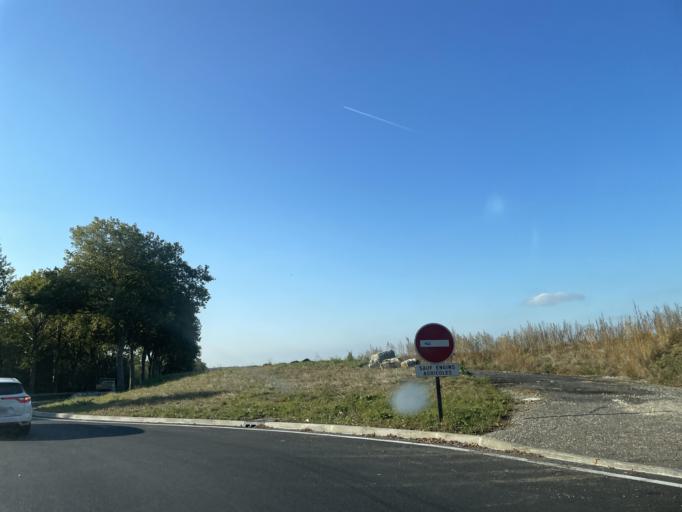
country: FR
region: Ile-de-France
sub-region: Departement de Seine-et-Marne
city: La Chapelle-sur-Crecy
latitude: 48.8481
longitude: 2.9406
